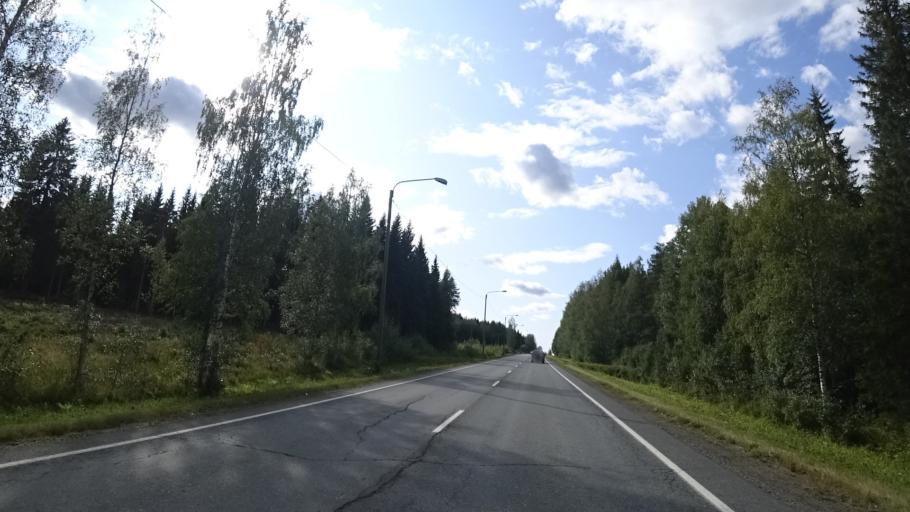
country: FI
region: North Karelia
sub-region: Keski-Karjala
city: Tohmajaervi
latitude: 62.2217
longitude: 30.3711
